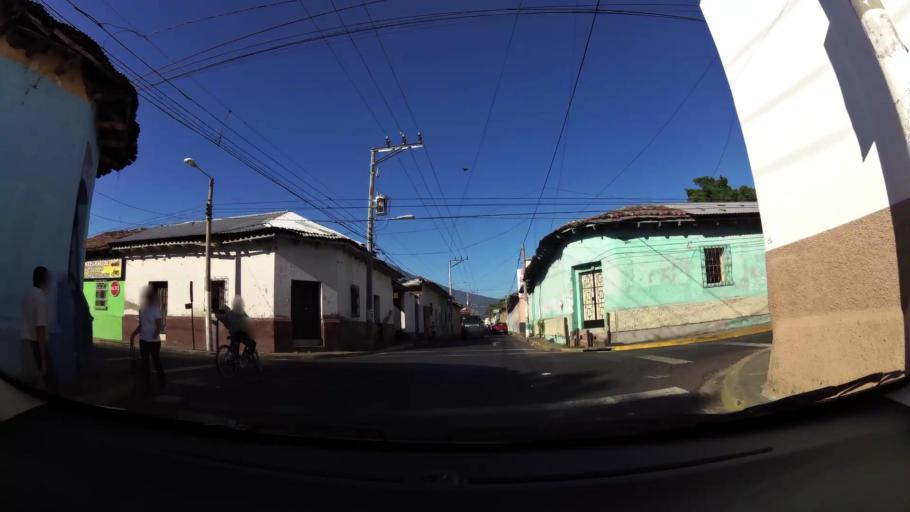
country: SV
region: San Miguel
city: San Miguel
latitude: 13.4777
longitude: -88.1747
